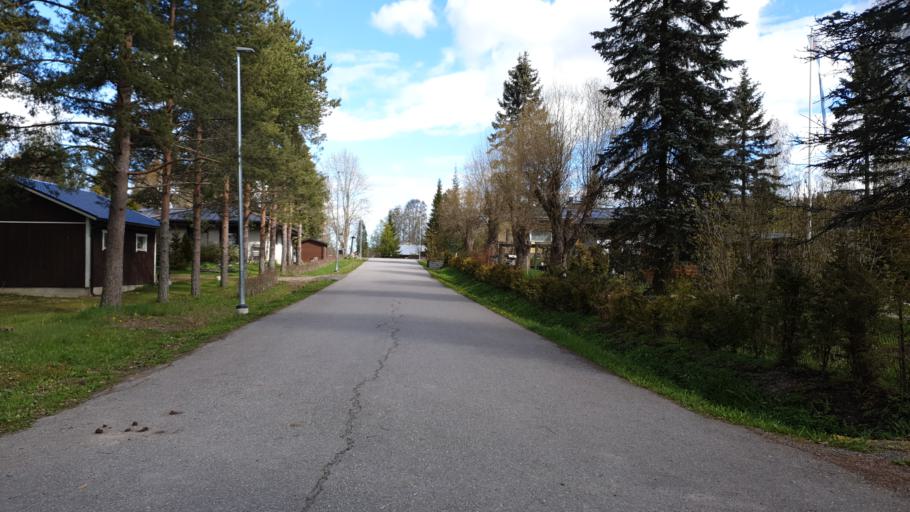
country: FI
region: Uusimaa
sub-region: Helsinki
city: Nurmijaervi
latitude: 60.3418
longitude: 24.8315
